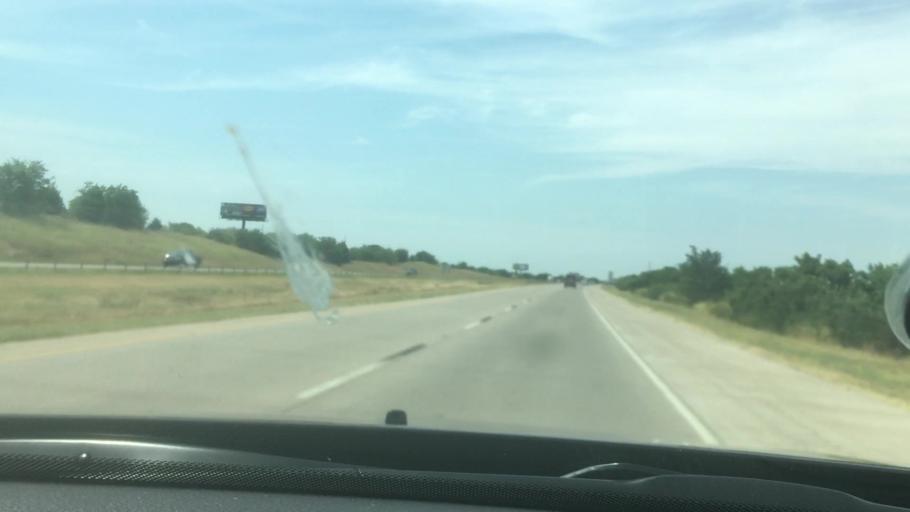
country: US
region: Oklahoma
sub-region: Carter County
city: Ardmore
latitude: 34.2961
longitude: -97.1595
